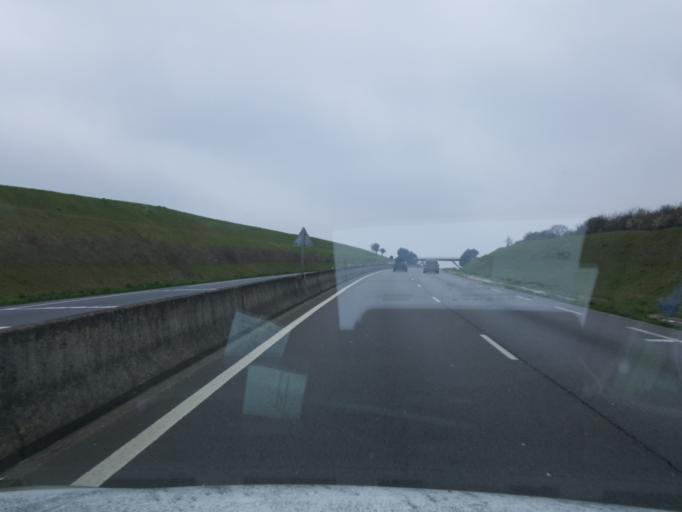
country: FR
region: Centre
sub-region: Departement d'Eure-et-Loir
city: Garnay
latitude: 48.7206
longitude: 1.3476
